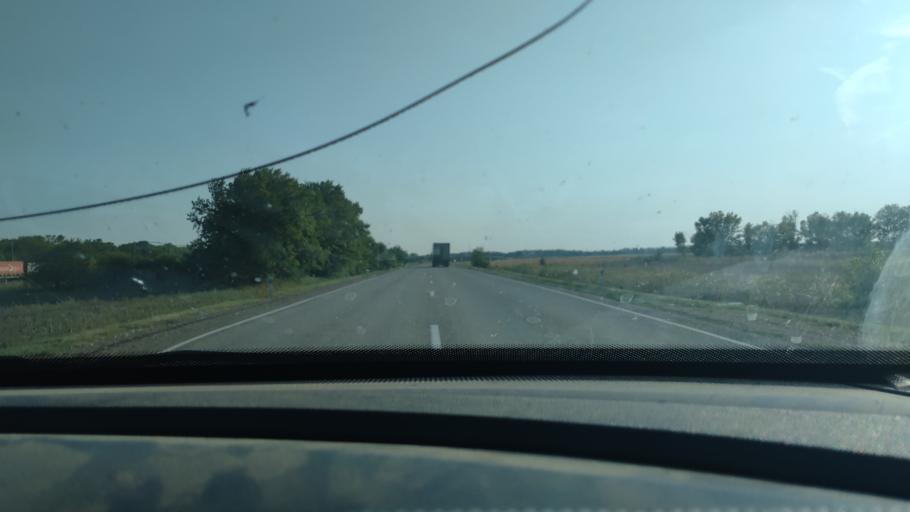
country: RU
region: Krasnodarskiy
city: Starominskaya
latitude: 46.4320
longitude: 39.0166
